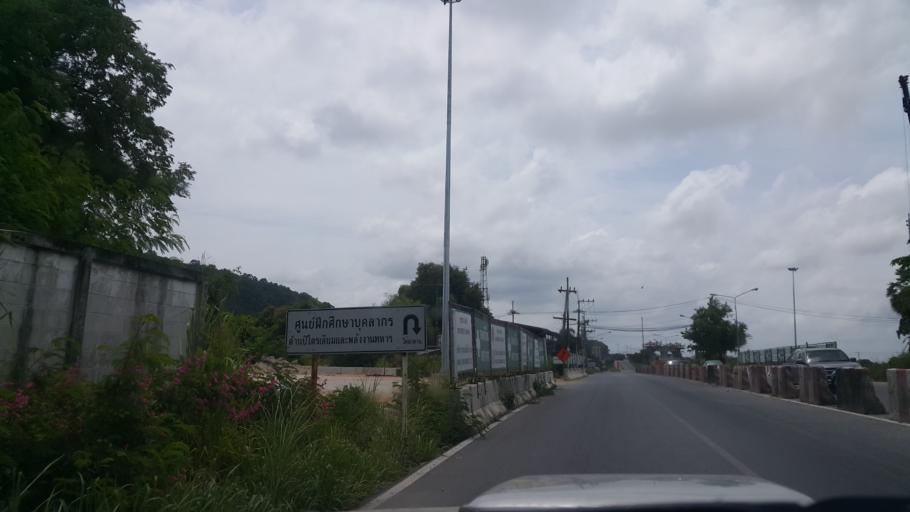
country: TH
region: Rayong
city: Ban Chang
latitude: 12.7098
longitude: 101.0269
